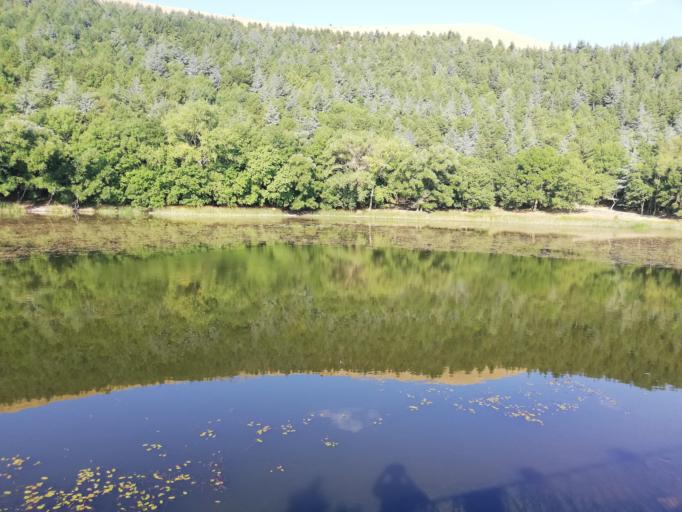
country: IT
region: Apulia
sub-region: Provincia di Foggia
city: Biccari
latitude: 41.3702
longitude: 15.1717
